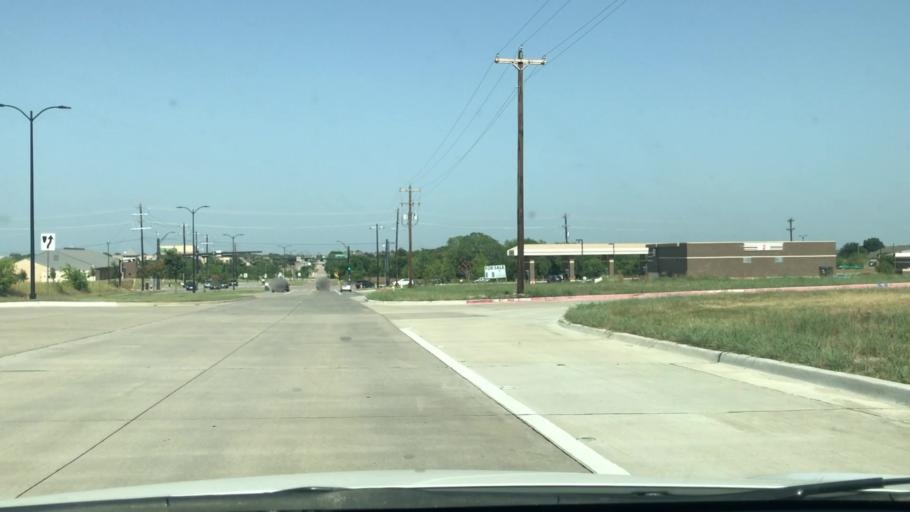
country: US
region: Texas
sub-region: Collin County
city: Frisco
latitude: 33.1377
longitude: -96.7525
